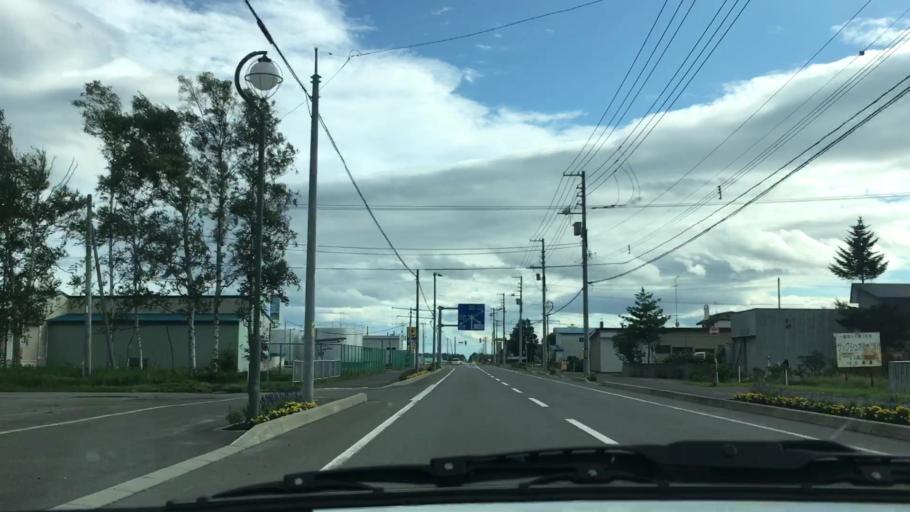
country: JP
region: Hokkaido
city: Otofuke
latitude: 43.2269
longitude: 143.2938
